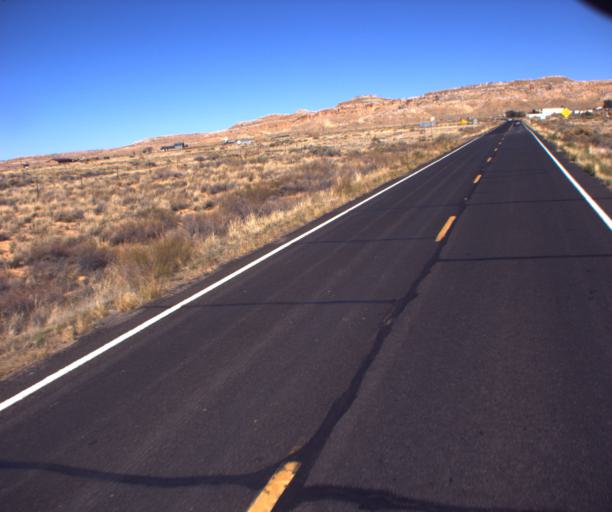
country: US
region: Arizona
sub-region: Navajo County
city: First Mesa
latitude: 35.7857
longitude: -110.4994
